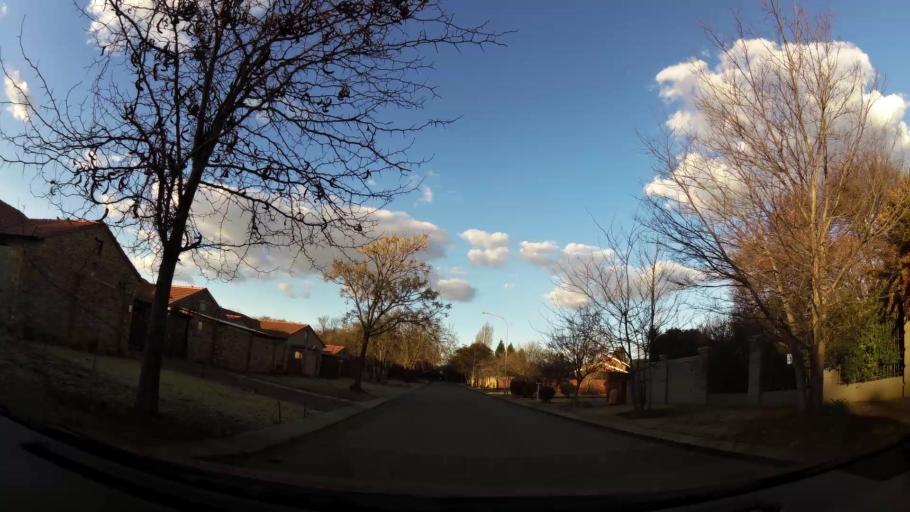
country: ZA
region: North-West
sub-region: Dr Kenneth Kaunda District Municipality
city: Potchefstroom
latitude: -26.6802
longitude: 27.1044
